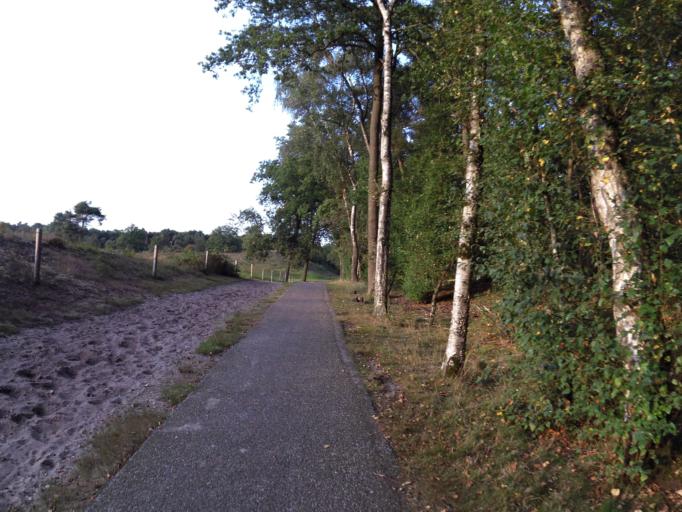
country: NL
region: Gelderland
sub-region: Gemeente Nijmegen
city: Lindenholt
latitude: 51.7816
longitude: 5.8087
